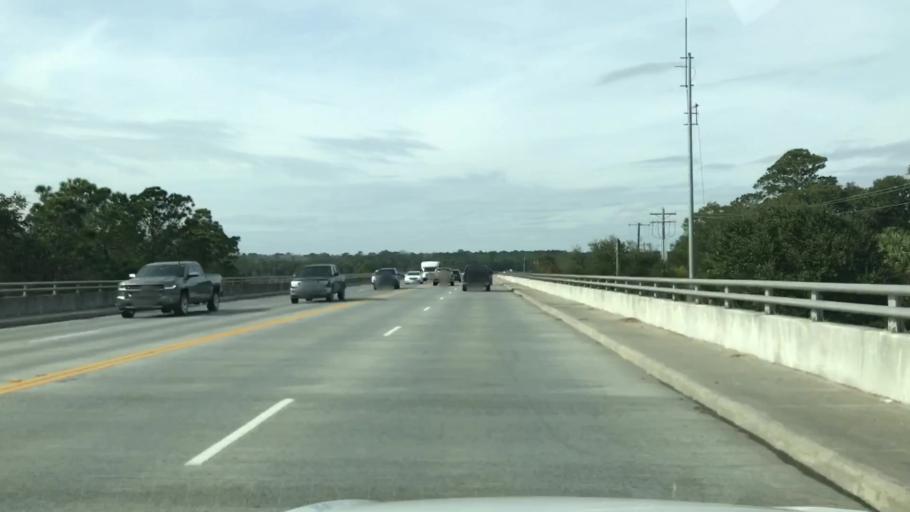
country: US
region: South Carolina
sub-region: Charleston County
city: Charleston
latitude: 32.7519
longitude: -80.0178
